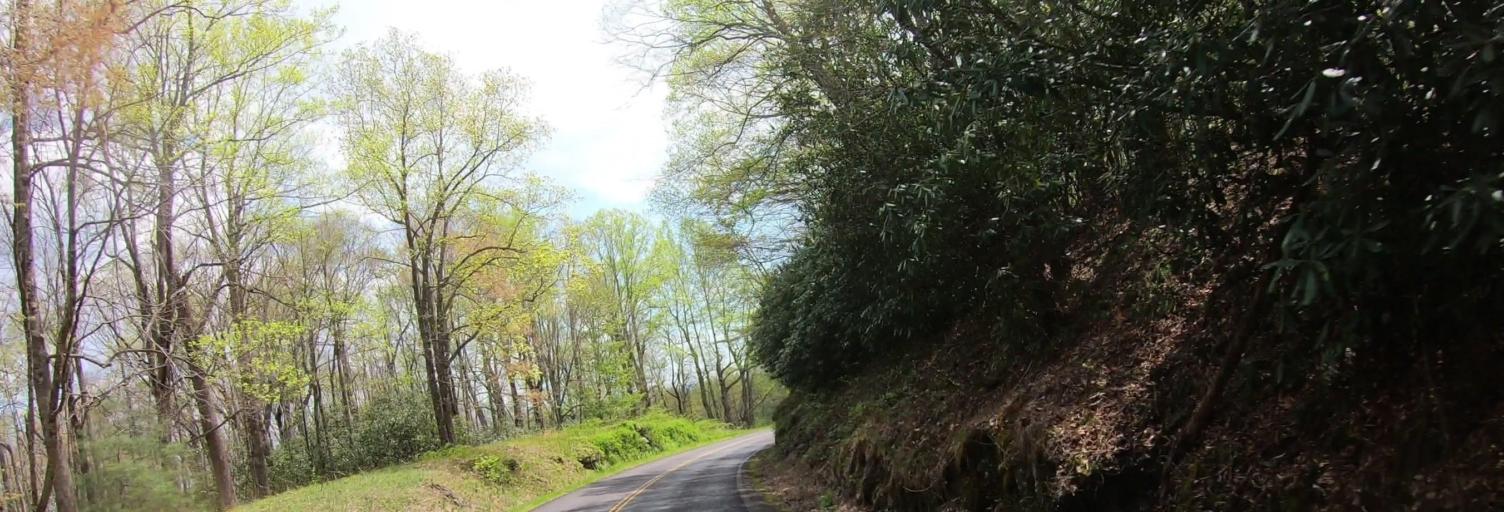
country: US
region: Virginia
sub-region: Carroll County
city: Cana
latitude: 36.6716
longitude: -80.6361
